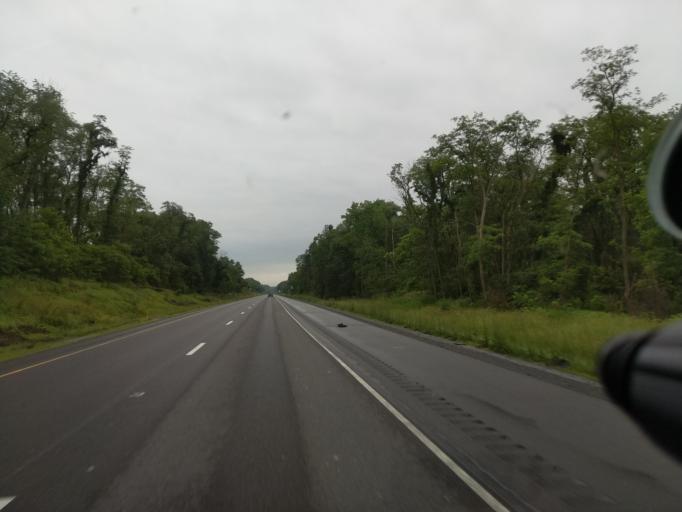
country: US
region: Pennsylvania
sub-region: Clinton County
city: Mill Hall
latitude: 41.0498
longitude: -77.4459
